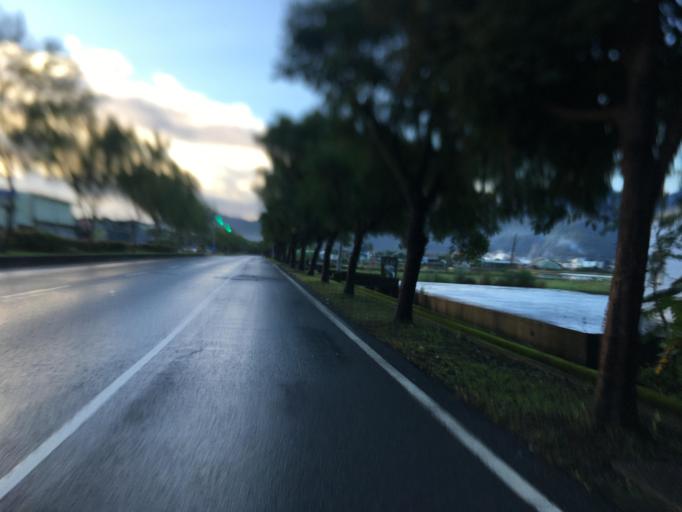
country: TW
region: Taiwan
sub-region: Yilan
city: Yilan
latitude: 24.6465
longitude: 121.7850
